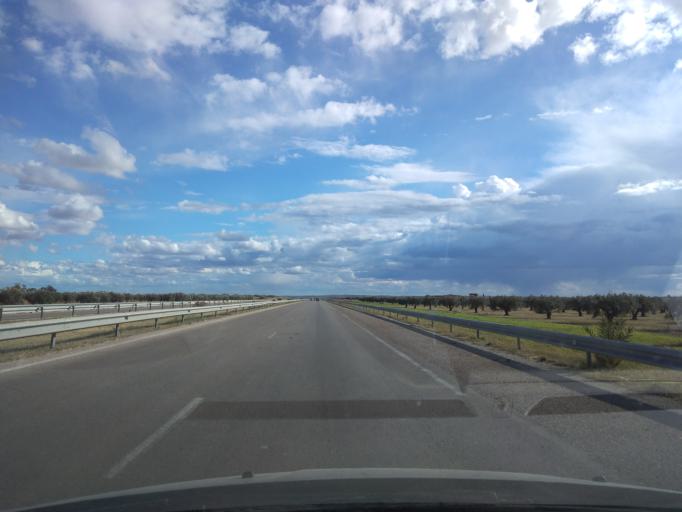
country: TN
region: Al Munastir
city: Manzil Kamil
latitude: 35.6179
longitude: 10.5951
